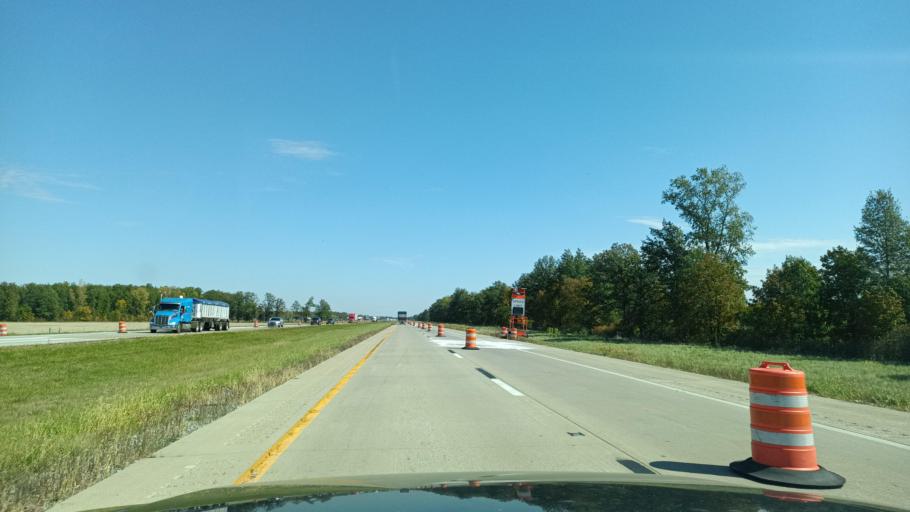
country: US
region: Ohio
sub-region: Paulding County
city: Paulding
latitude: 41.2460
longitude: -84.4965
